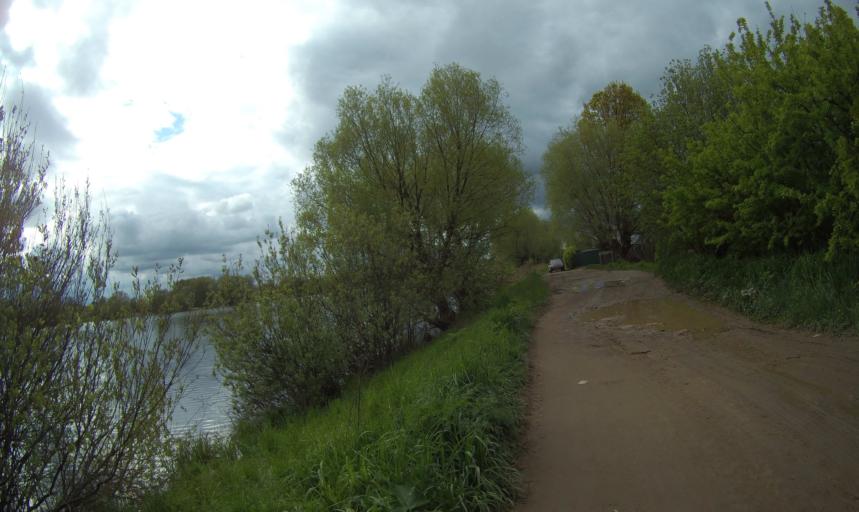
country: RU
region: Moskovskaya
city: Rechitsy
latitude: 55.5944
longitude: 38.5144
